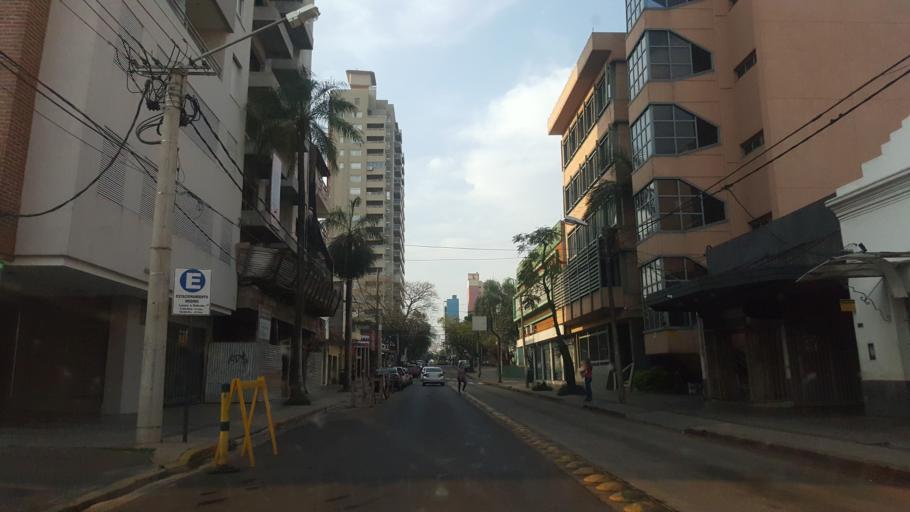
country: AR
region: Misiones
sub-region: Departamento de Capital
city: Posadas
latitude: -27.3711
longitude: -55.8973
